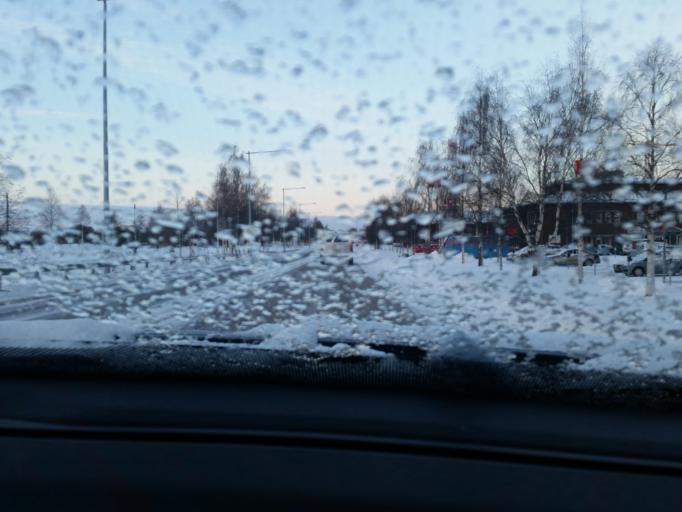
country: SE
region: Norrbotten
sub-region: Pitea Kommun
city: Pitea
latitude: 65.3130
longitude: 21.4836
